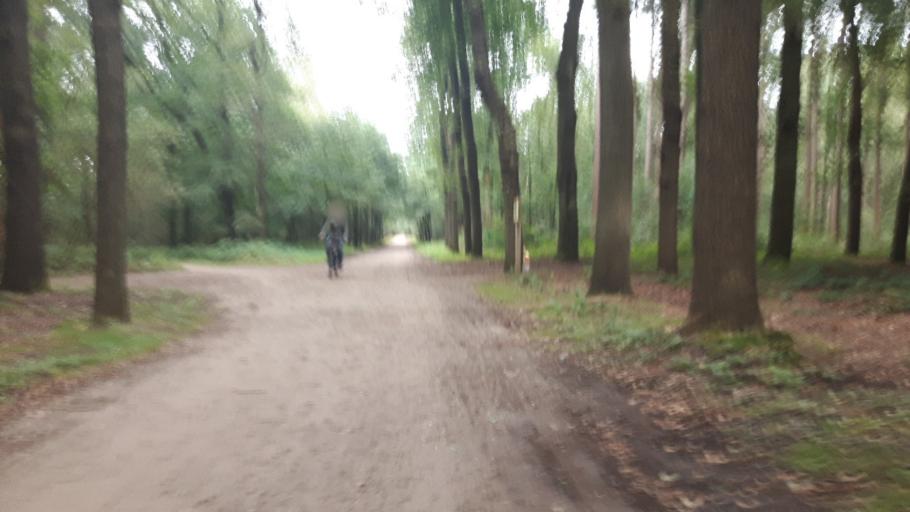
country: NL
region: Gelderland
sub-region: Gemeente Ermelo
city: Ermelo
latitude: 52.2796
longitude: 5.6150
